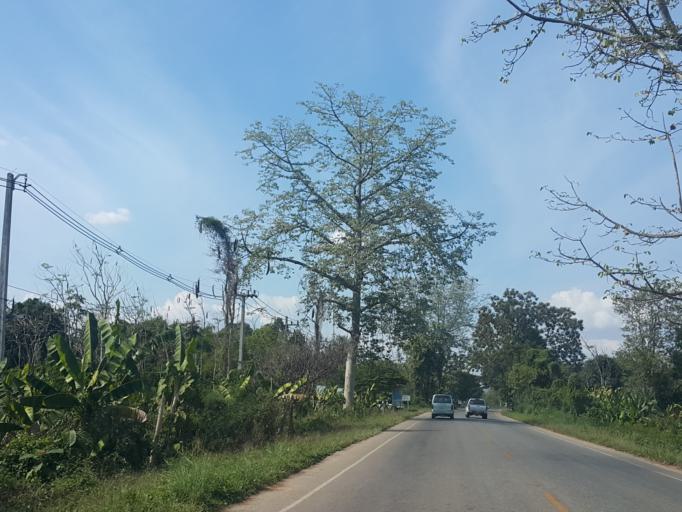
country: TH
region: Sukhothai
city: Sawankhalok
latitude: 17.2513
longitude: 99.8448
